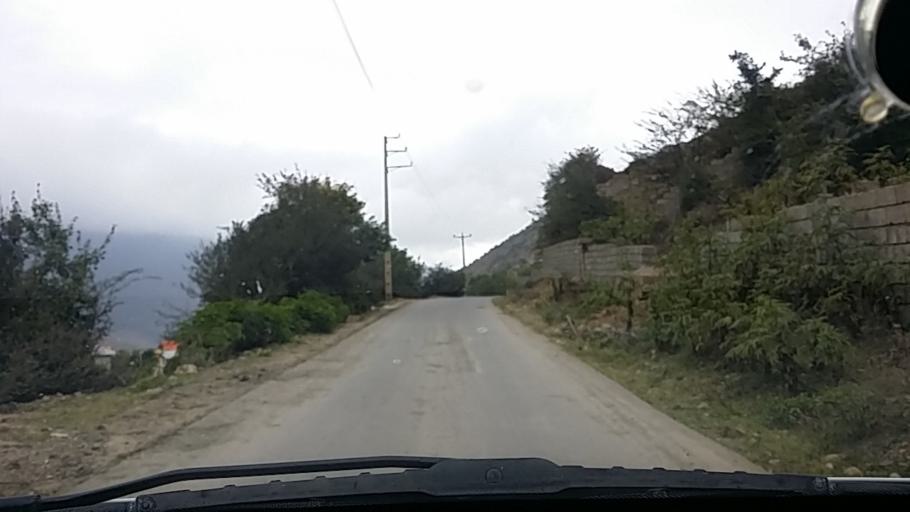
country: IR
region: Mazandaran
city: `Abbasabad
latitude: 36.4707
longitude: 51.1398
